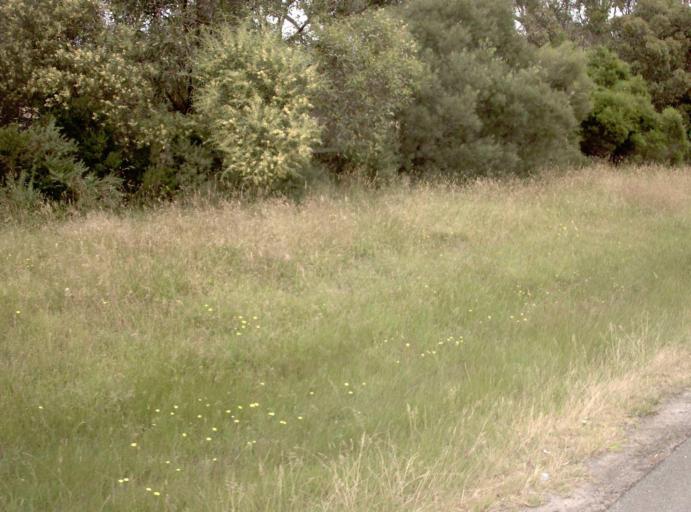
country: AU
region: Victoria
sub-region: Mornington Peninsula
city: Safety Beach
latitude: -38.3070
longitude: 145.0307
